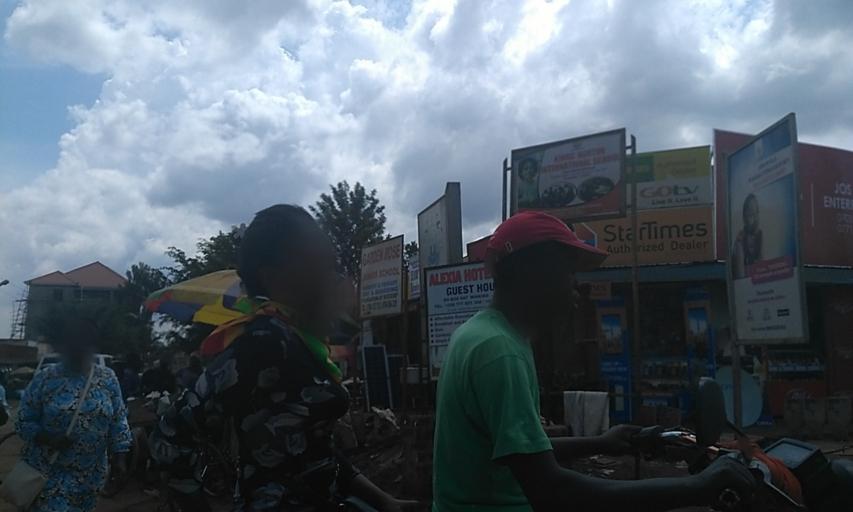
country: UG
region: Central Region
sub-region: Wakiso District
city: Wakiso
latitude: 0.3980
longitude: 32.4779
